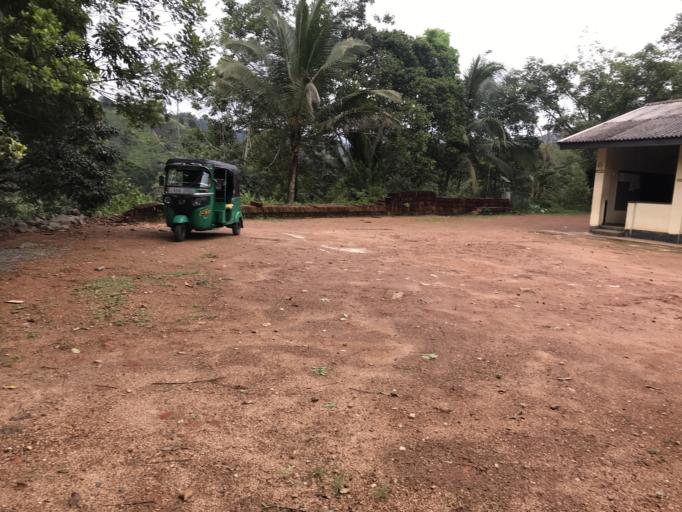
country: LK
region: Sabaragamuwa
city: Ratnapura
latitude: 6.4492
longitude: 80.5118
